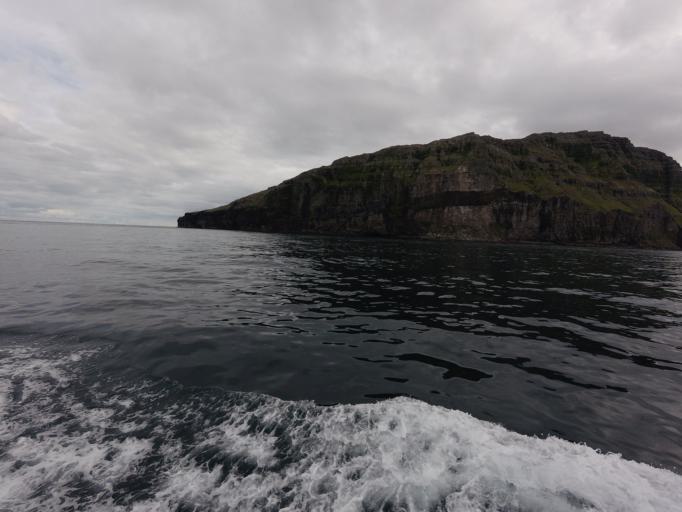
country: FO
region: Nordoyar
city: Klaksvik
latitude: 62.3091
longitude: -6.3470
